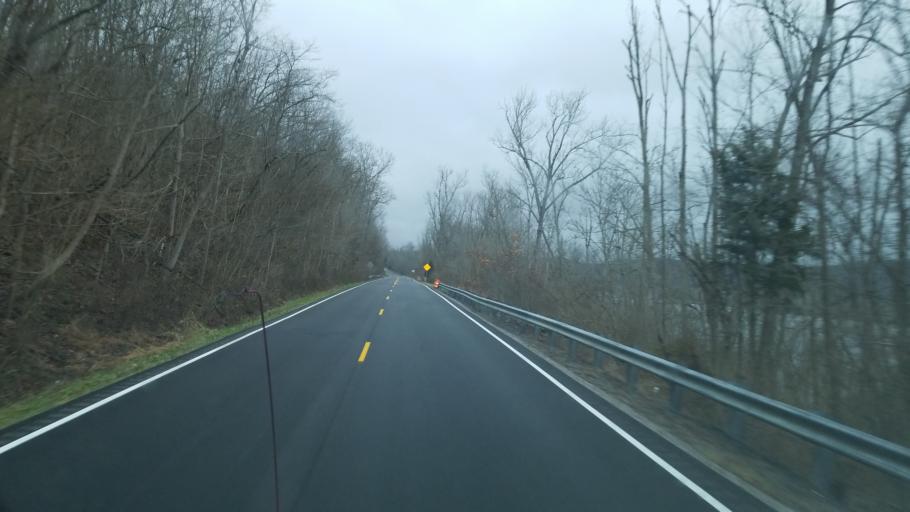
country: US
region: Kentucky
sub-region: Bracken County
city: Augusta
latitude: 38.7715
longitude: -83.9327
